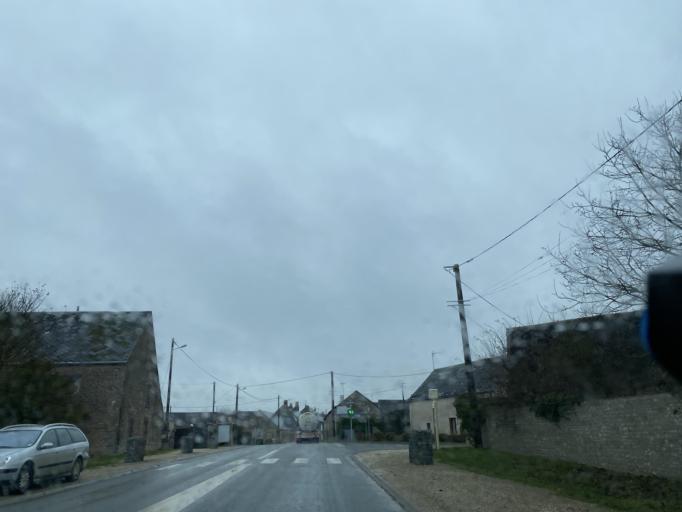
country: FR
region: Centre
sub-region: Departement d'Eure-et-Loir
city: Janville
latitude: 48.2058
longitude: 1.8227
